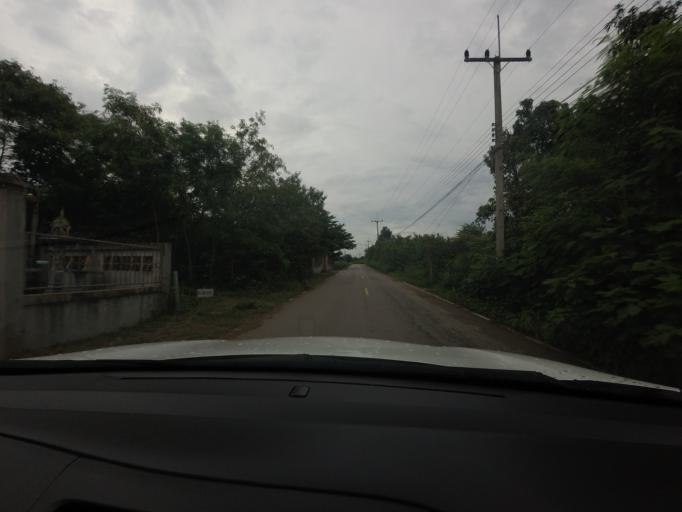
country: TH
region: Nakhon Ratchasima
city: Pak Chong
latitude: 14.6498
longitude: 101.4203
